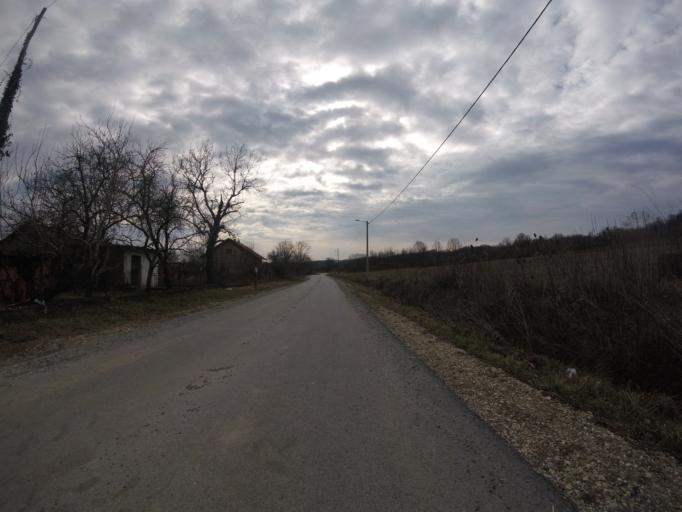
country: HR
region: Sisacko-Moslavacka
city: Glina
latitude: 45.4471
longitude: 16.0690
